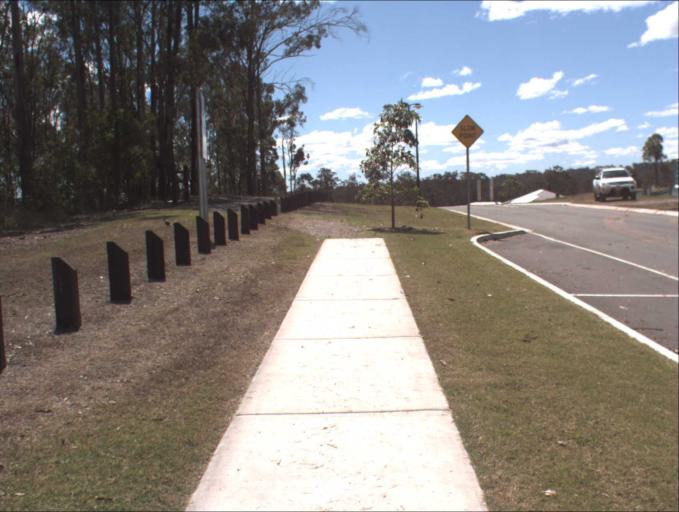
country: AU
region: Queensland
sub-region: Logan
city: Cedar Vale
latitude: -27.8660
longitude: 153.0533
